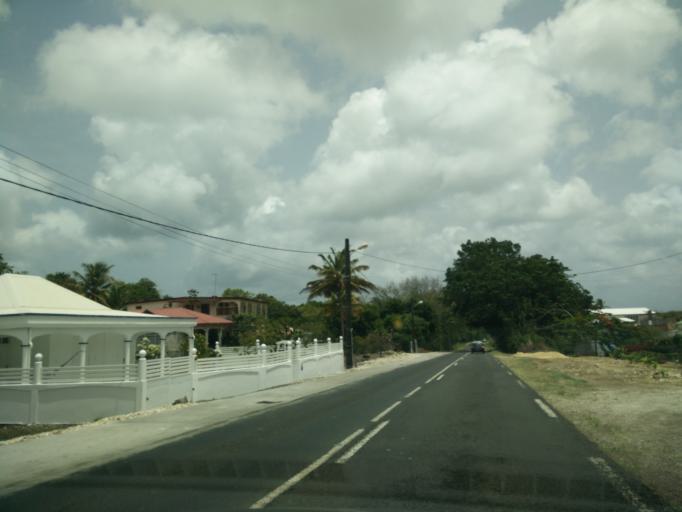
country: GP
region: Guadeloupe
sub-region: Guadeloupe
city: Petit-Canal
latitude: 16.3991
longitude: -61.4998
